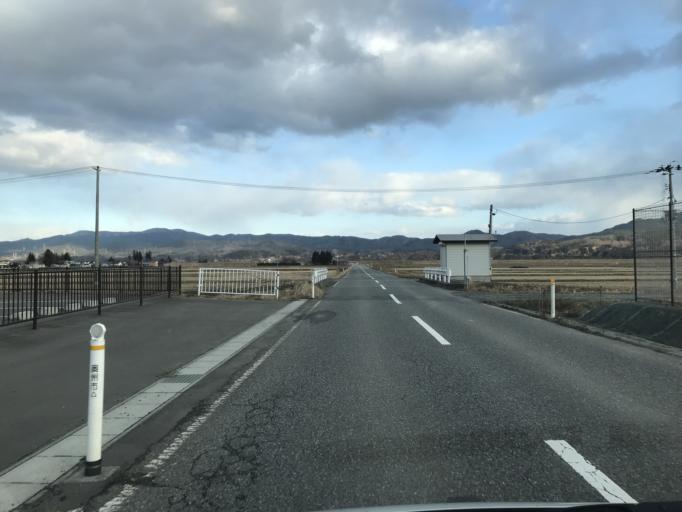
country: JP
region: Iwate
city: Mizusawa
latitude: 39.0581
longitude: 141.1442
